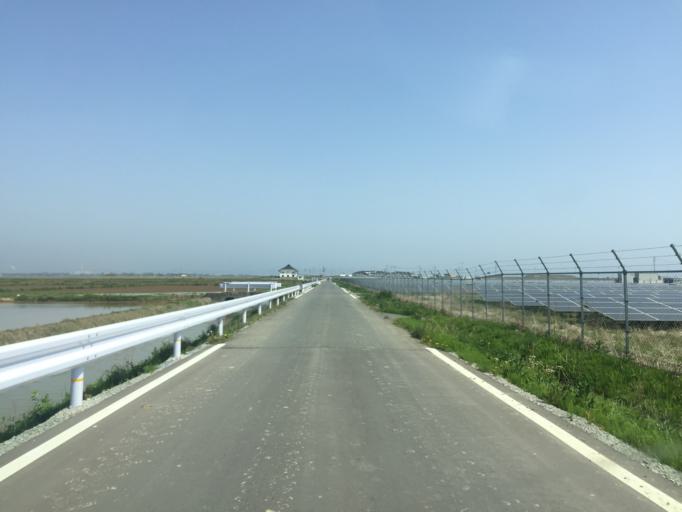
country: JP
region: Miyagi
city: Marumori
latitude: 37.7692
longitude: 140.9772
